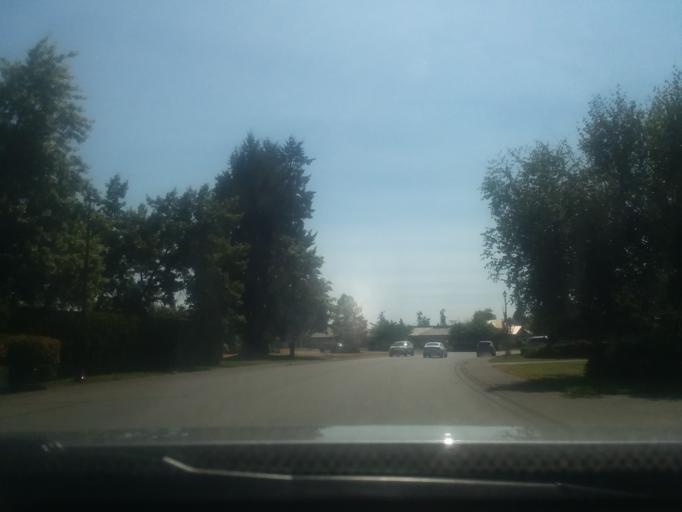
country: CA
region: British Columbia
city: Courtenay
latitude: 49.7114
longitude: -124.9596
